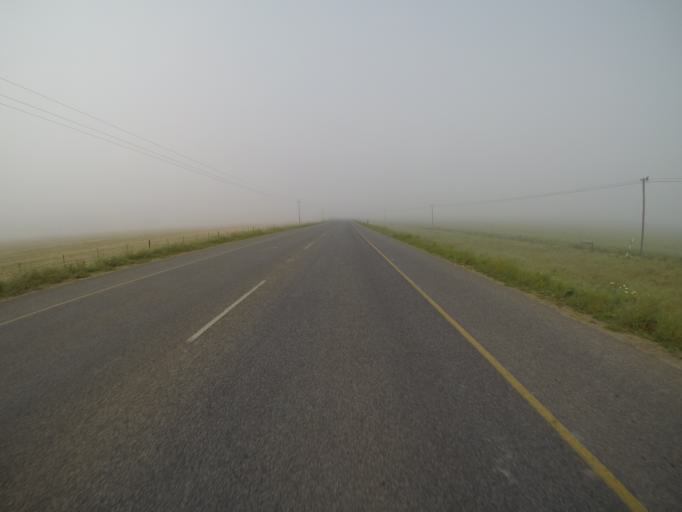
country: ZA
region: Western Cape
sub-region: City of Cape Town
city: Kraaifontein
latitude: -33.6761
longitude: 18.7066
